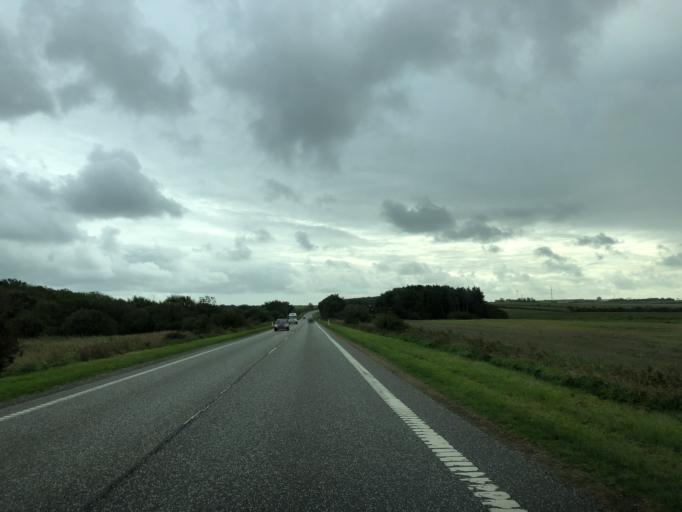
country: DK
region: North Denmark
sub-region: Thisted Kommune
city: Hurup
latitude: 56.7857
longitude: 8.4676
